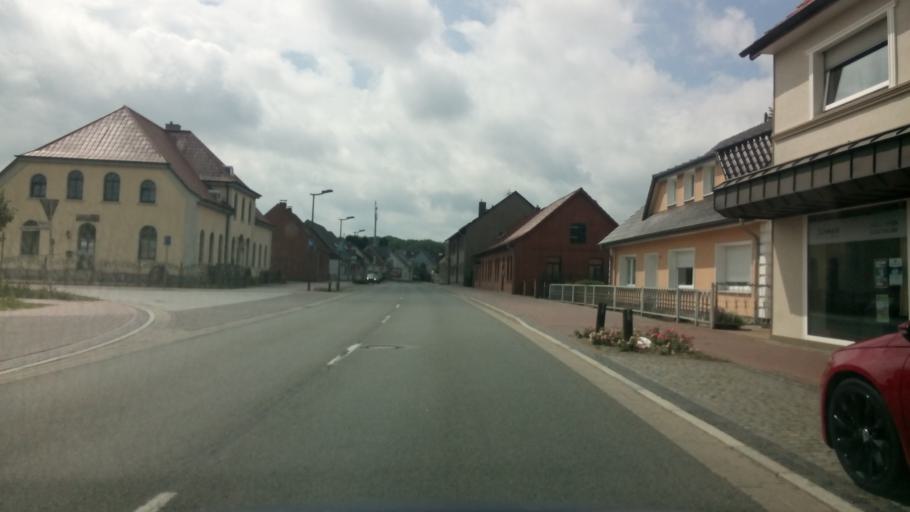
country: DE
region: Lower Saxony
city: Barnstorf
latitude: 52.7122
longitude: 8.5107
